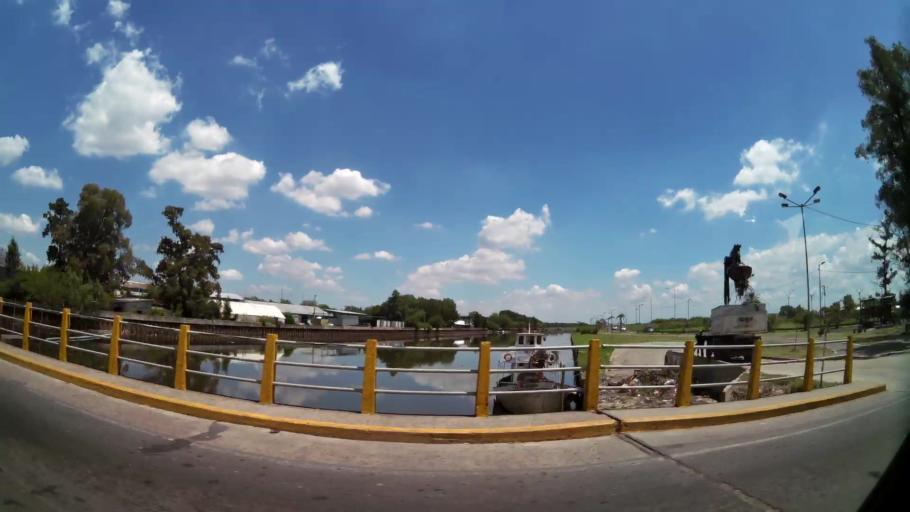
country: AR
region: Buenos Aires
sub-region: Partido de Tigre
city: Tigre
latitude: -34.4412
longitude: -58.5966
